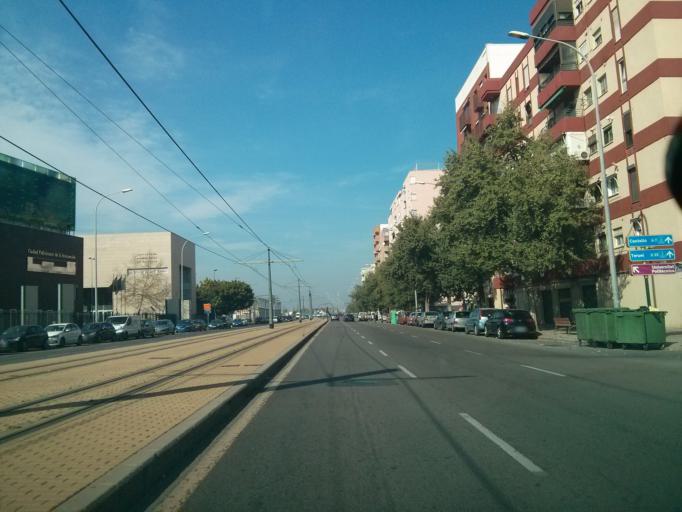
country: ES
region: Valencia
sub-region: Provincia de Valencia
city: Alboraya
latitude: 39.4779
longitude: -0.3331
